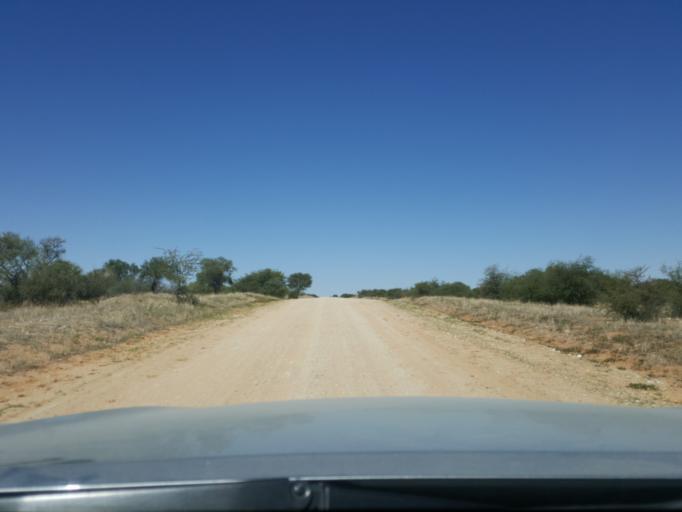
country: BW
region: Kgalagadi
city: Hukuntsi
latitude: -24.1046
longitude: 21.2319
